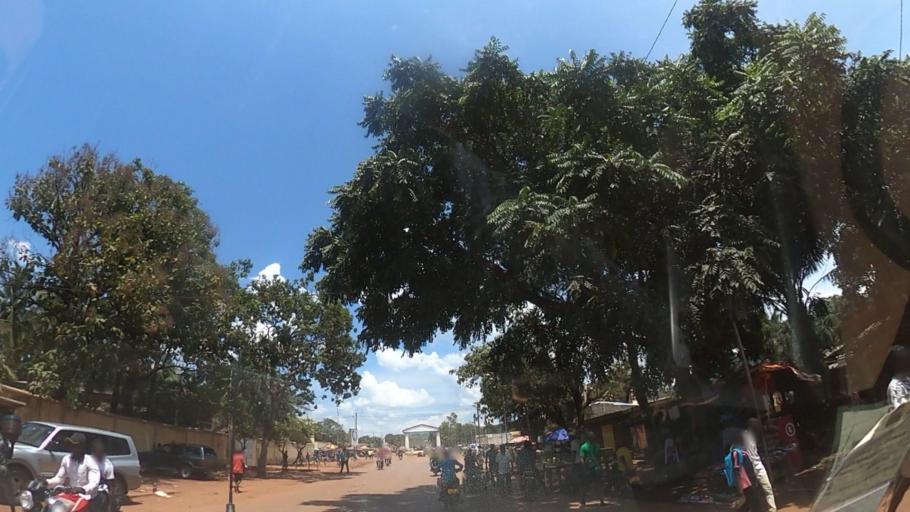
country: CF
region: Bangui
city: Bangui
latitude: 4.3648
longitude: 18.5614
